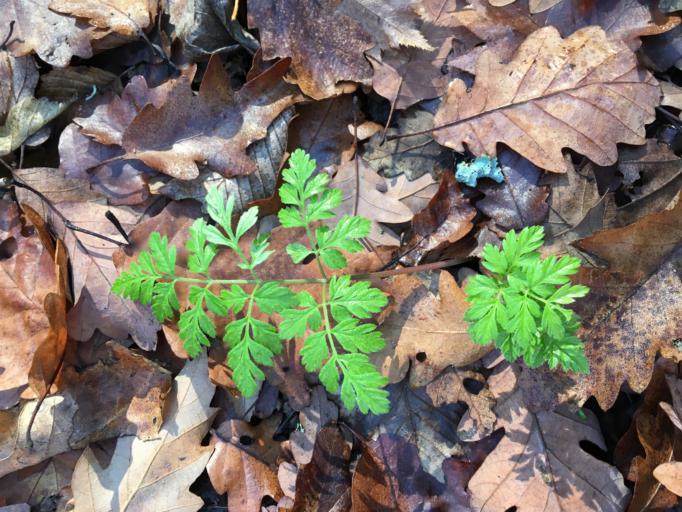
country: XK
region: Pristina
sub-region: Komuna e Prishtines
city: Pristina
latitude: 42.6718
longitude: 21.2231
